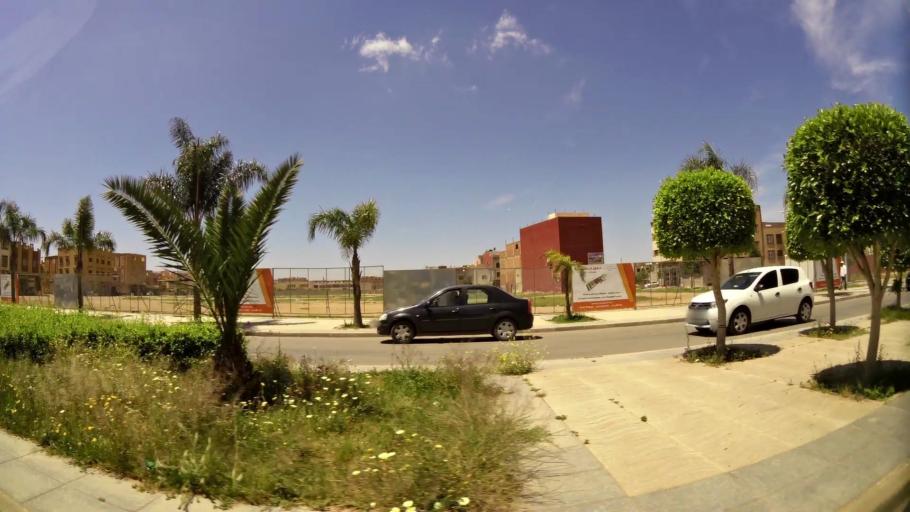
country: MA
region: Oriental
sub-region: Oujda-Angad
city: Oujda
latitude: 34.6633
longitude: -1.9379
